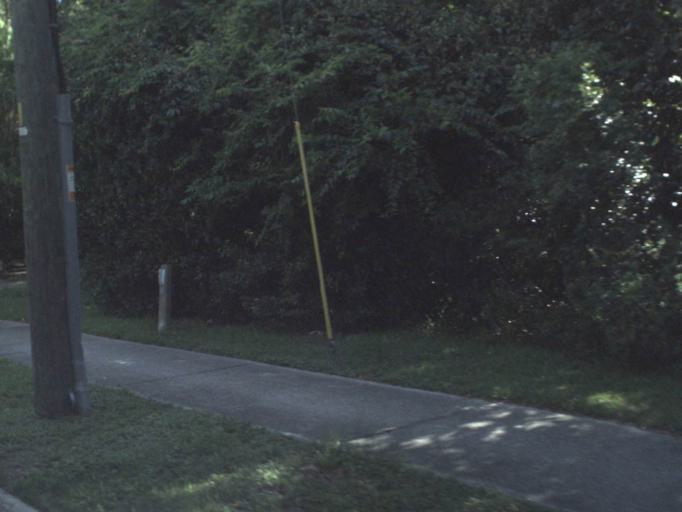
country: US
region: Florida
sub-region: Alachua County
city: Gainesville
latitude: 29.6831
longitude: -82.3307
